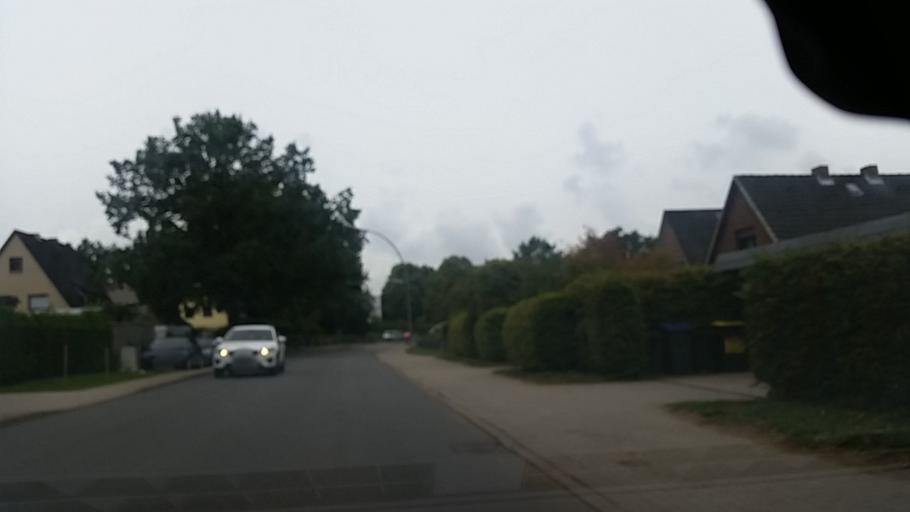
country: DE
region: Hamburg
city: Hummelsbuettel
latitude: 53.6890
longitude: 10.0472
